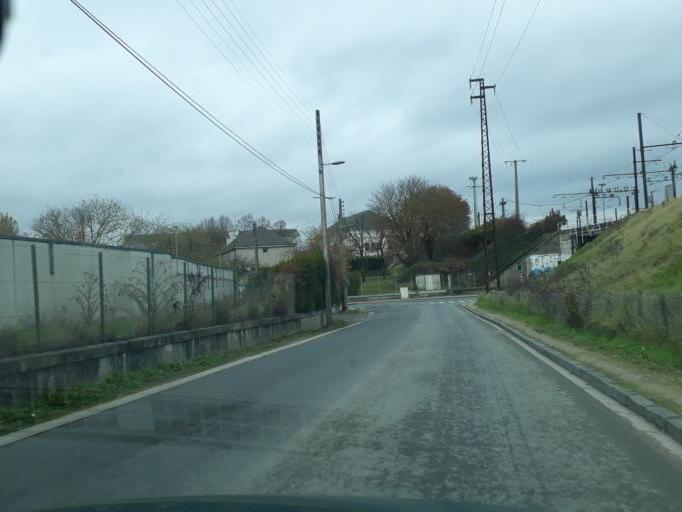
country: FR
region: Centre
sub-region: Departement du Loiret
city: Fleury-les-Aubrais
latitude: 47.9335
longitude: 1.9000
